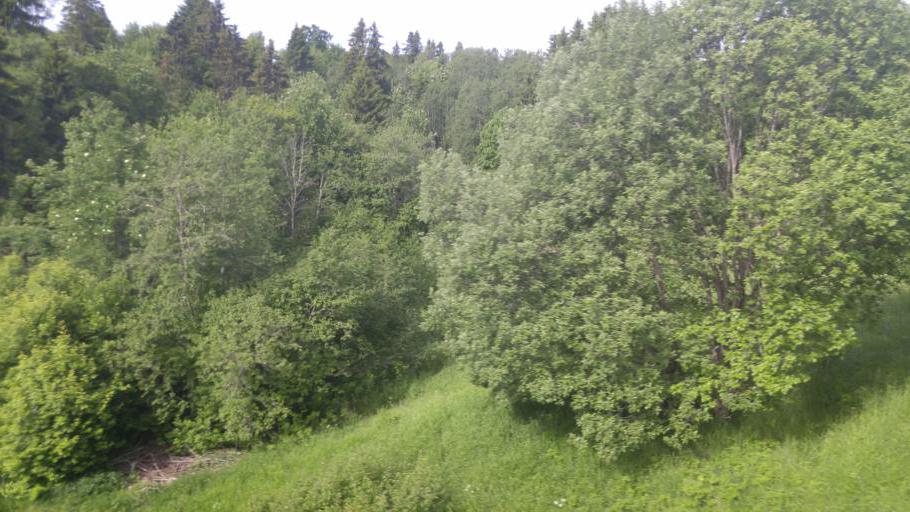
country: NO
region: Sor-Trondelag
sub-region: Trondheim
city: Trondheim
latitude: 63.3815
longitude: 10.3581
